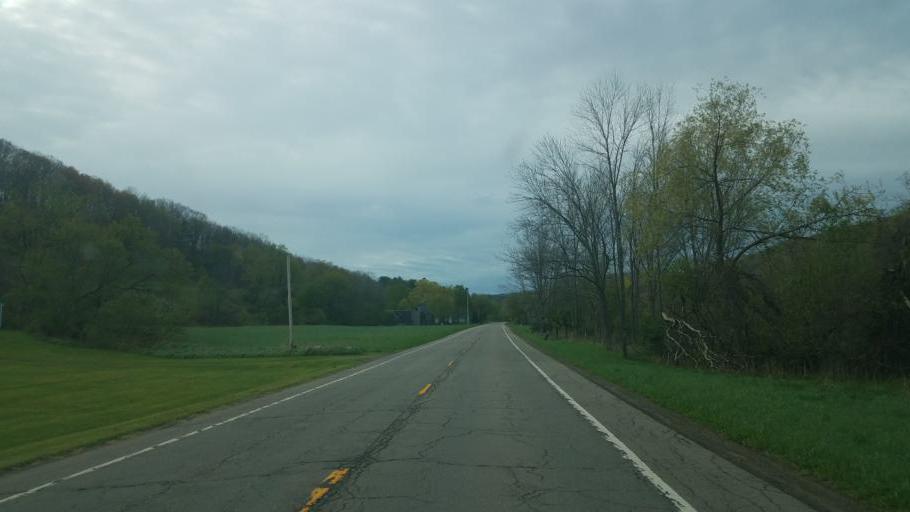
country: US
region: New York
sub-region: Steuben County
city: Canisteo
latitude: 42.2087
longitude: -77.5628
